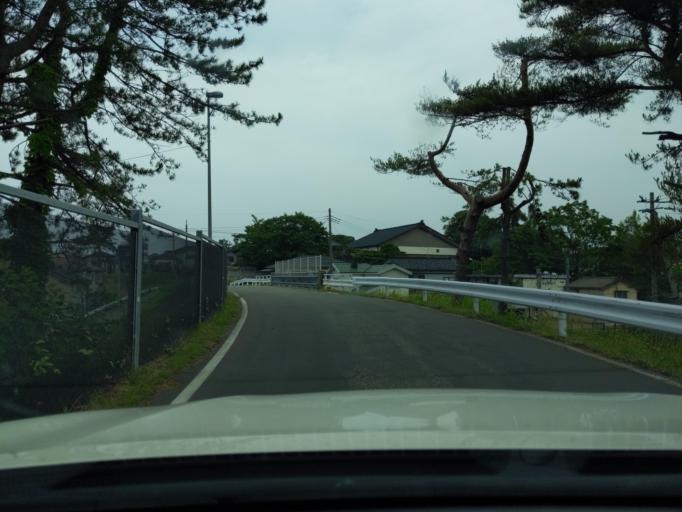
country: JP
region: Niigata
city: Kashiwazaki
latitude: 37.3616
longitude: 138.5403
